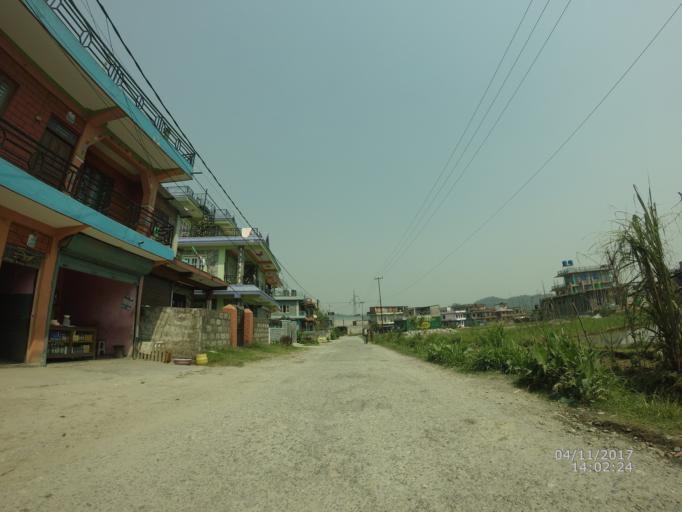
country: NP
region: Western Region
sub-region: Gandaki Zone
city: Pokhara
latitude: 28.1847
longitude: 84.0441
